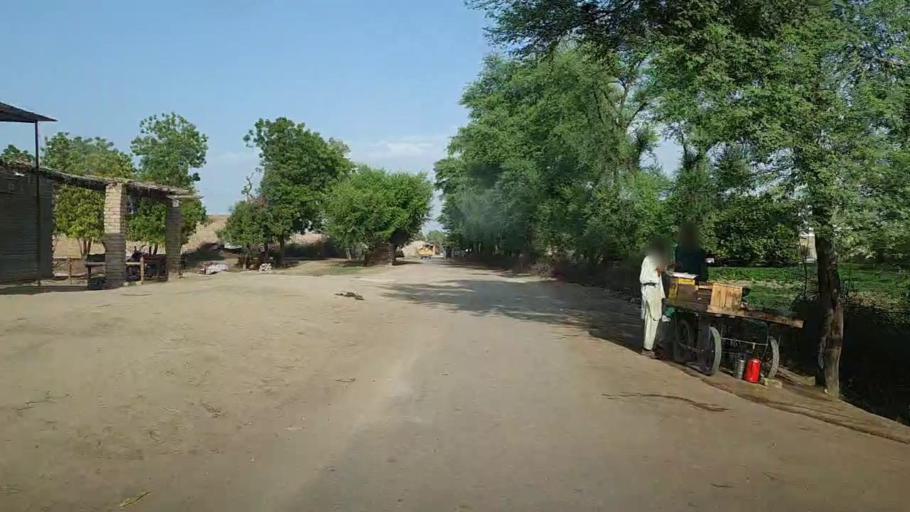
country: PK
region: Sindh
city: Khairpur
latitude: 28.0745
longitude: 69.8220
